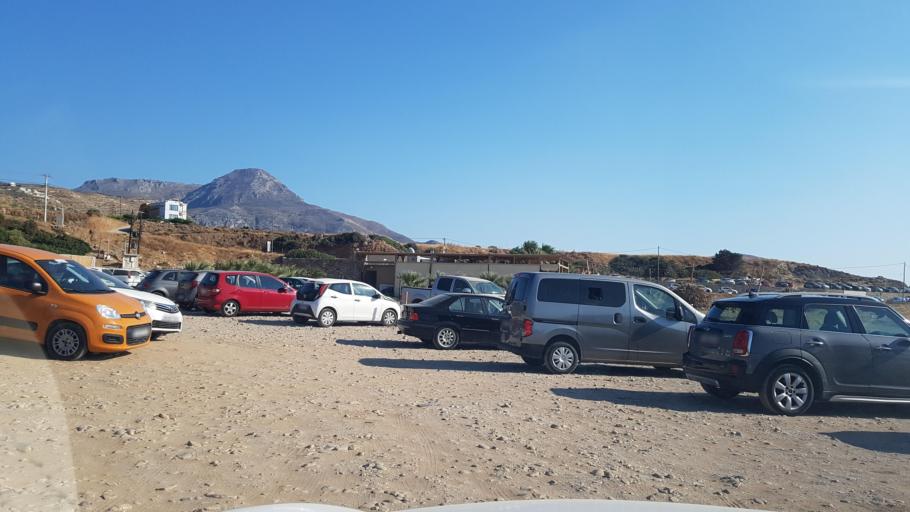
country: GR
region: Crete
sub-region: Nomos Chanias
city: Platanos
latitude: 35.4906
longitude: 23.5817
